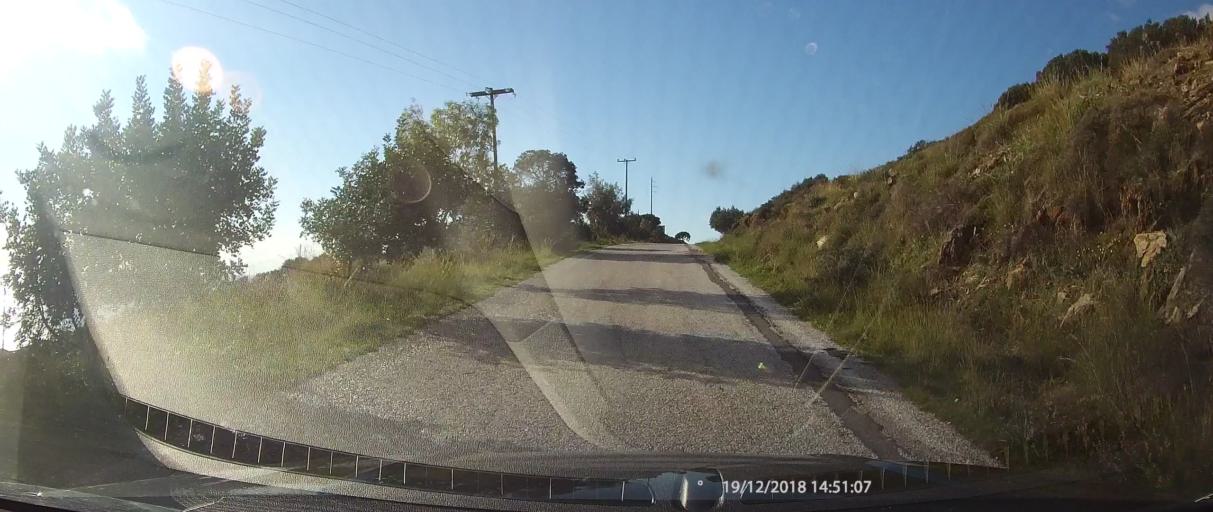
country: GR
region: Peloponnese
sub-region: Nomos Lakonias
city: Gytheio
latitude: 36.4571
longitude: 22.4513
